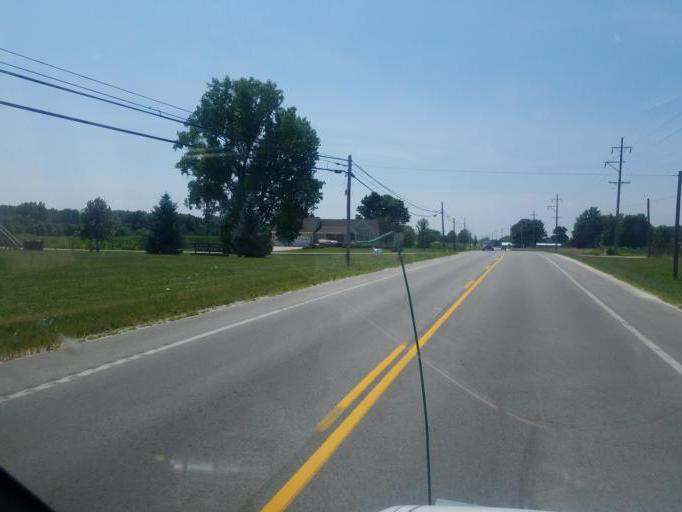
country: US
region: Ohio
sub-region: Auglaize County
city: Saint Marys
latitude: 40.5511
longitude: -84.4643
